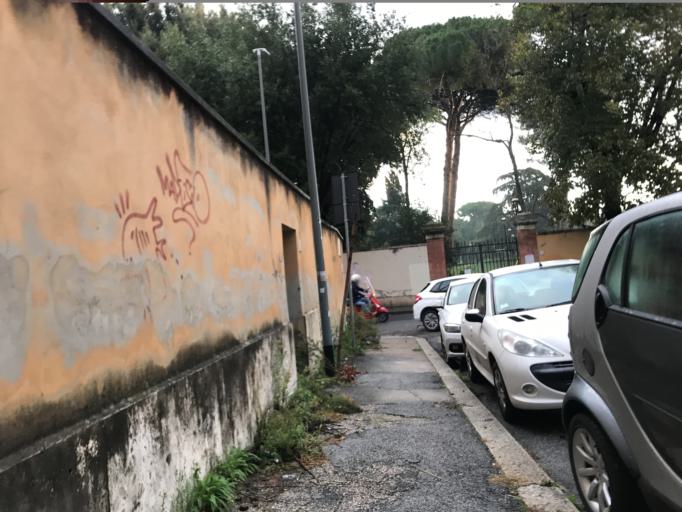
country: IT
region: Latium
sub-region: Citta metropolitana di Roma Capitale
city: Rome
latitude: 41.9122
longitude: 12.5106
